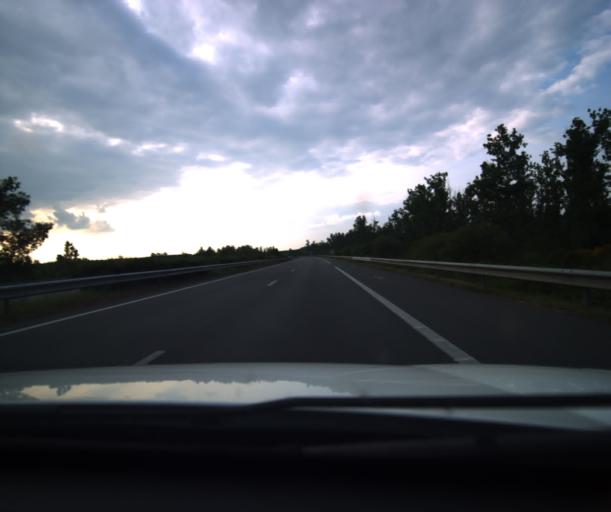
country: FR
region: Midi-Pyrenees
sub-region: Departement du Tarn-et-Garonne
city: Montech
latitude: 44.0019
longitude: 1.2245
